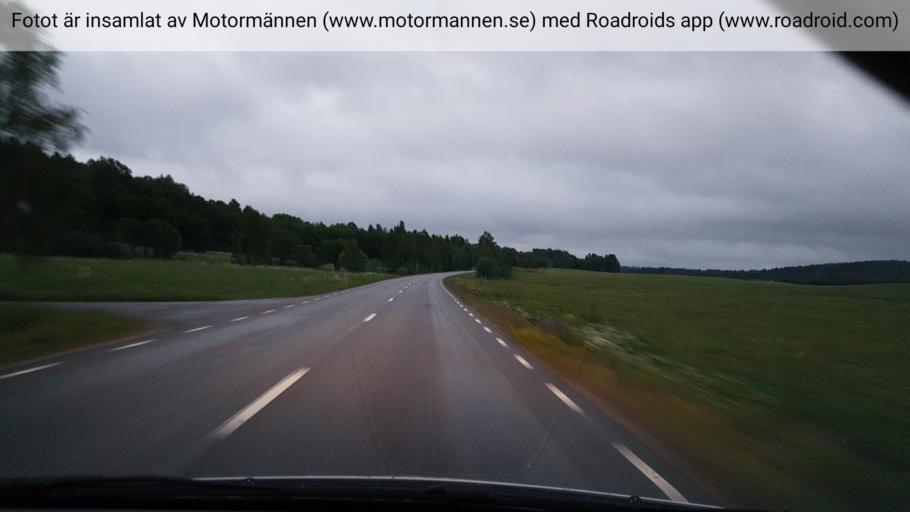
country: SE
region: Vaestmanland
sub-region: Skinnskattebergs Kommun
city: Skinnskatteberg
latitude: 59.8943
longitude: 15.5924
